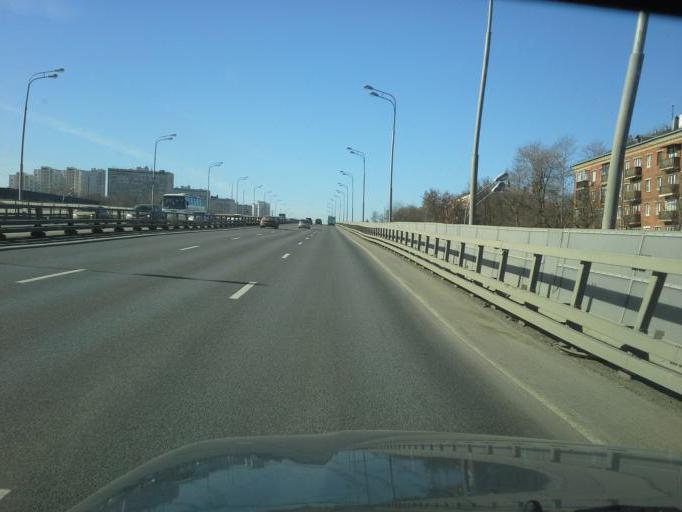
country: RU
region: Moskovskaya
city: Bol'shaya Setun'
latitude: 55.7173
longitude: 37.4088
